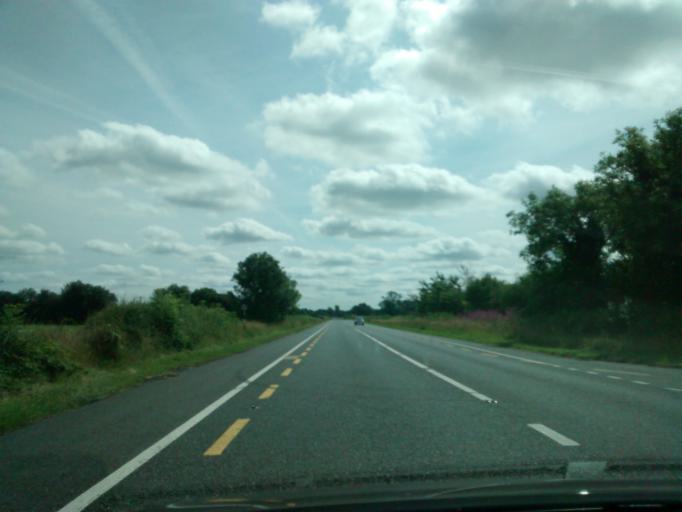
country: IE
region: Leinster
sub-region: Uibh Fhaili
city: Clara
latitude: 53.3695
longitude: -7.6489
